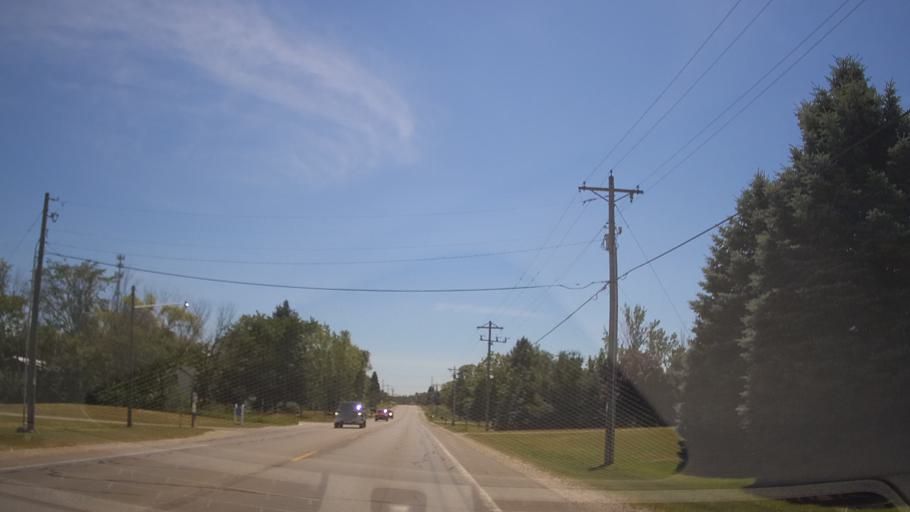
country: US
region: Michigan
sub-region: Grand Traverse County
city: Traverse City
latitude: 44.6729
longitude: -85.6900
